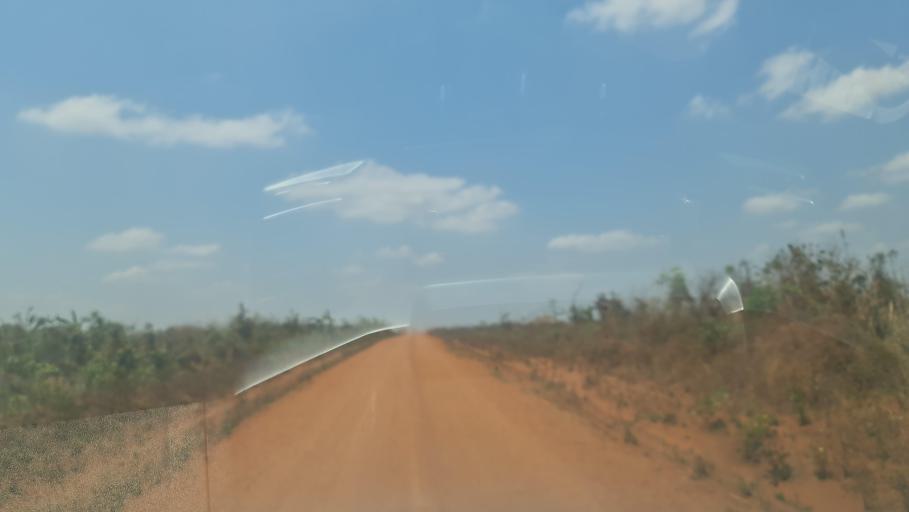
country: MW
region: Southern Region
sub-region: Nsanje District
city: Nsanje
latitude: -17.3421
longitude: 35.7336
